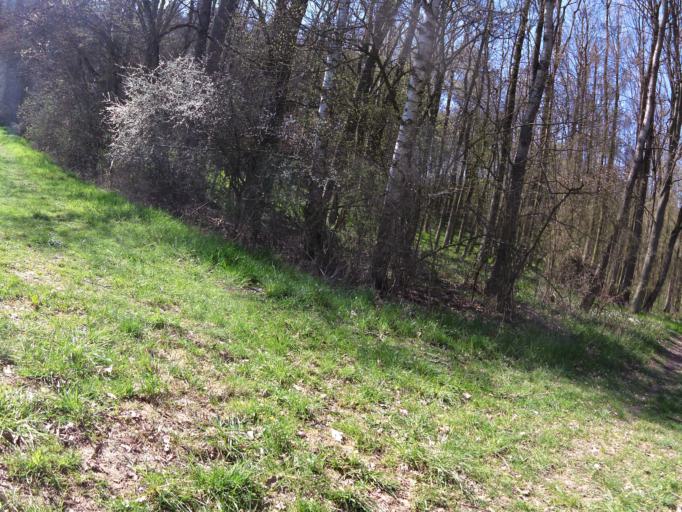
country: DE
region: Bavaria
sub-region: Regierungsbezirk Unterfranken
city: Kurnach
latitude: 49.8267
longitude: 10.0492
